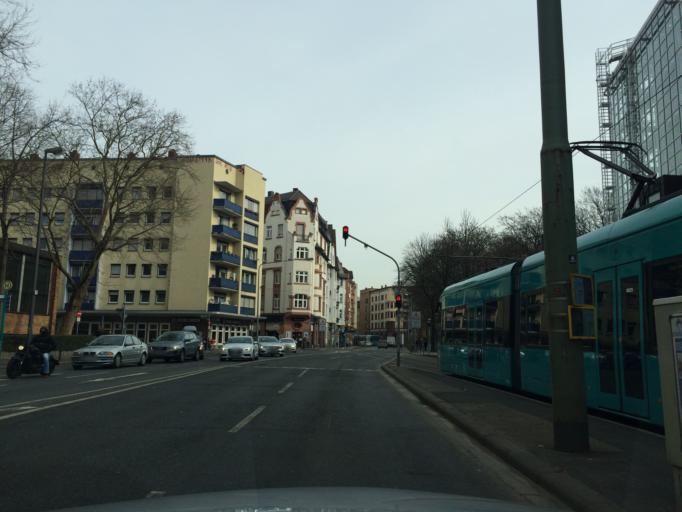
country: DE
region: Hesse
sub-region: Regierungsbezirk Darmstadt
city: Frankfurt am Main
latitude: 50.1126
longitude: 8.6886
